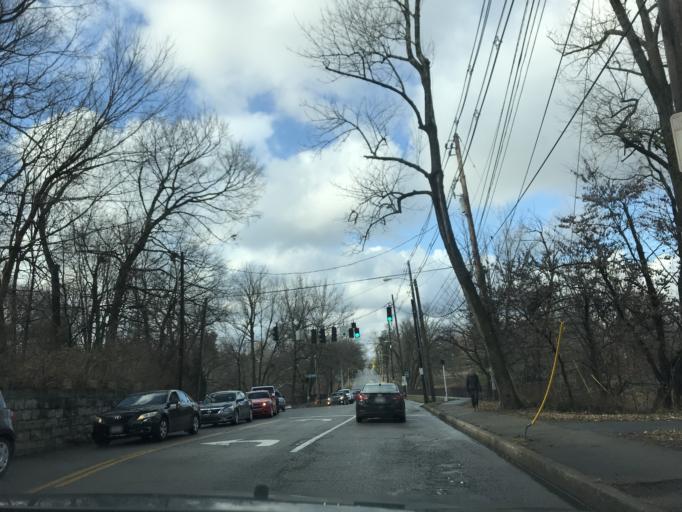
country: US
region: Kentucky
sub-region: Jefferson County
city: Audubon Park
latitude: 38.2300
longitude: -85.7160
